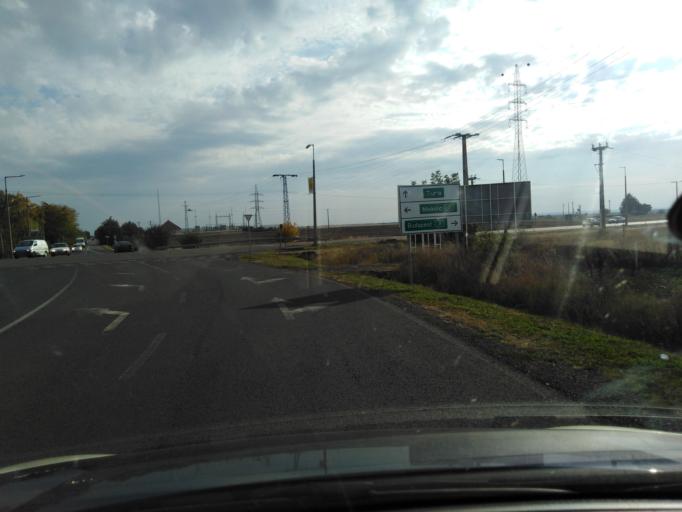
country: HU
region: Heves
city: Hatvan
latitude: 47.6622
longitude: 19.6433
